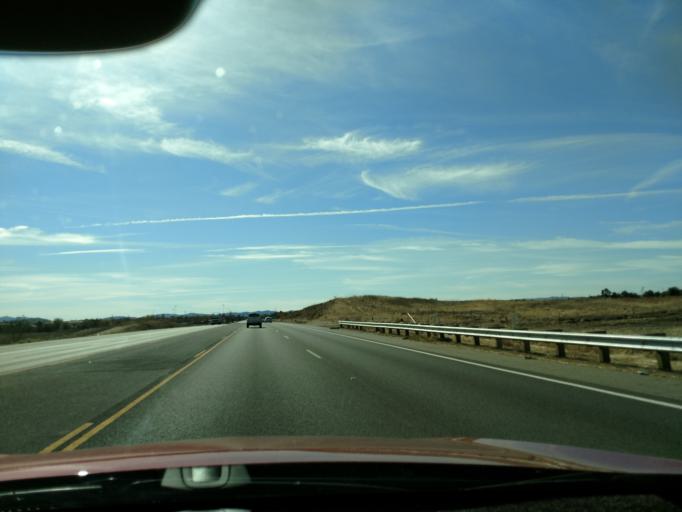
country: US
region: California
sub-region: Riverside County
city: Winchester
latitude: 33.6241
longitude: -117.0962
